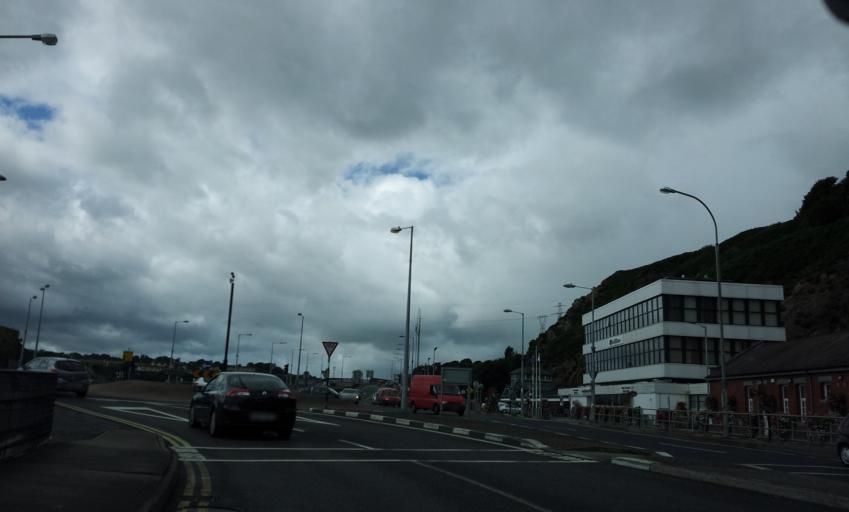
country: IE
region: Munster
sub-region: Waterford
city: Waterford
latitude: 52.2659
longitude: -7.1171
